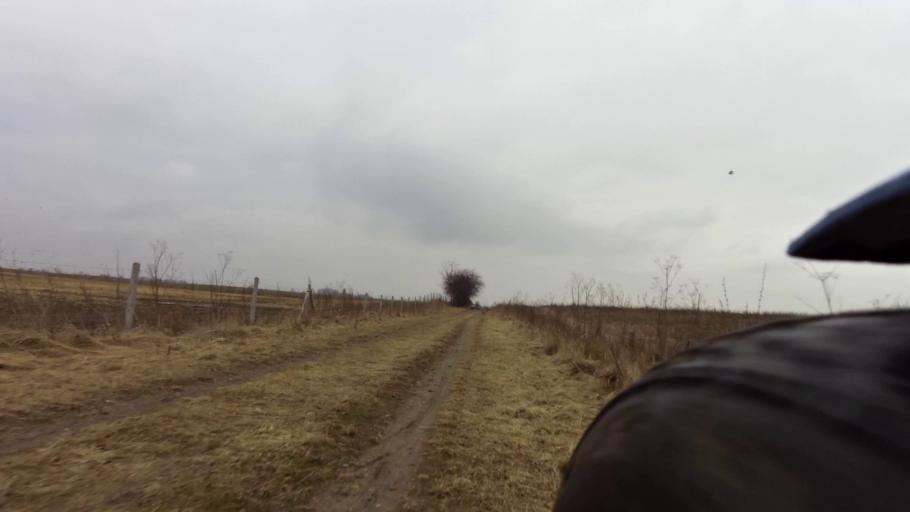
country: PL
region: West Pomeranian Voivodeship
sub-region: Powiat walecki
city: Walcz
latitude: 53.2416
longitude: 16.4685
